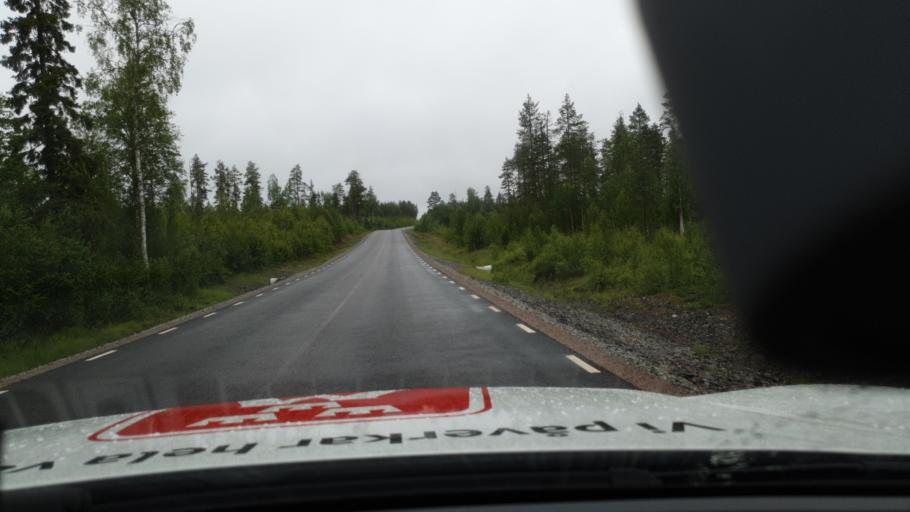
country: SE
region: Norrbotten
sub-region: Overtornea Kommun
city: OEvertornea
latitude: 66.5647
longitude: 23.3331
